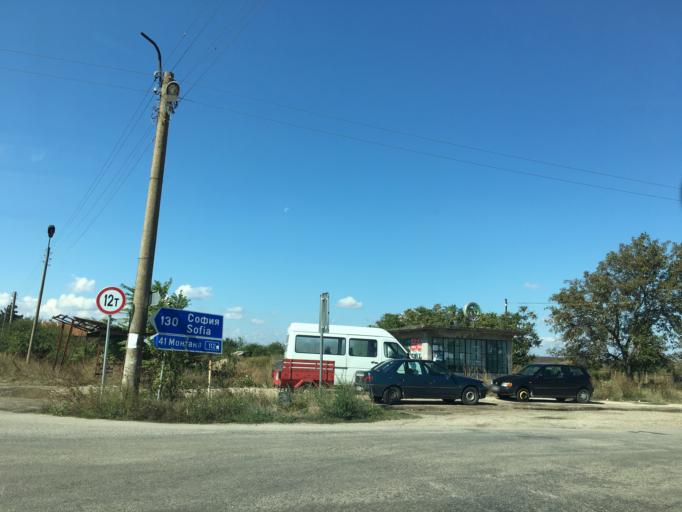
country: BG
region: Montana
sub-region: Obshtina Brusartsi
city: Brusartsi
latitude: 43.6993
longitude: 23.0104
